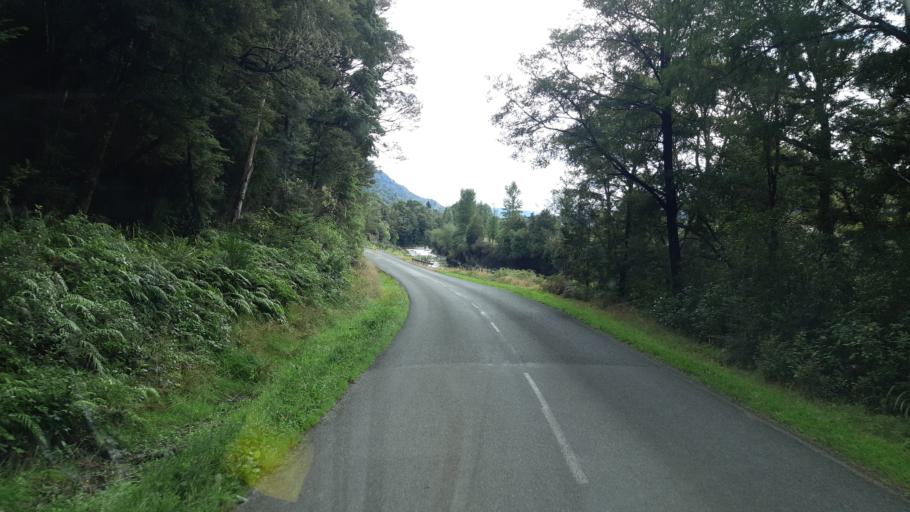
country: NZ
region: West Coast
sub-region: Buller District
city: Westport
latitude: -41.7810
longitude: 172.3709
